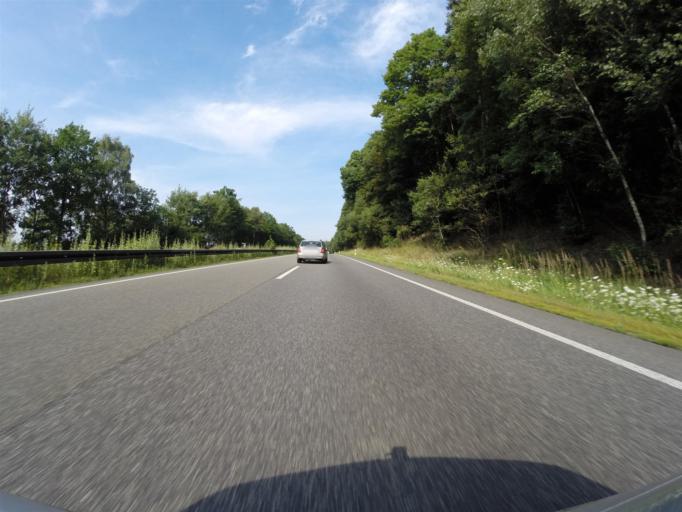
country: DE
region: Thuringia
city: Grossensee
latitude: 50.9387
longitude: 9.9303
